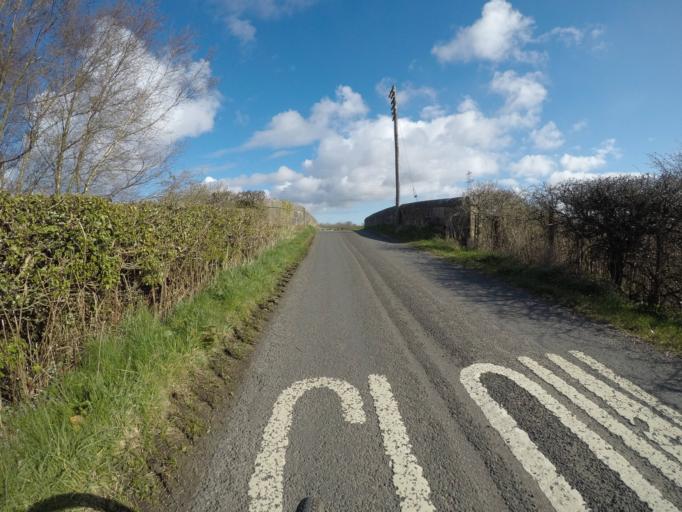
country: GB
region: Scotland
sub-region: North Ayrshire
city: Irvine
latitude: 55.6588
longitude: -4.6542
